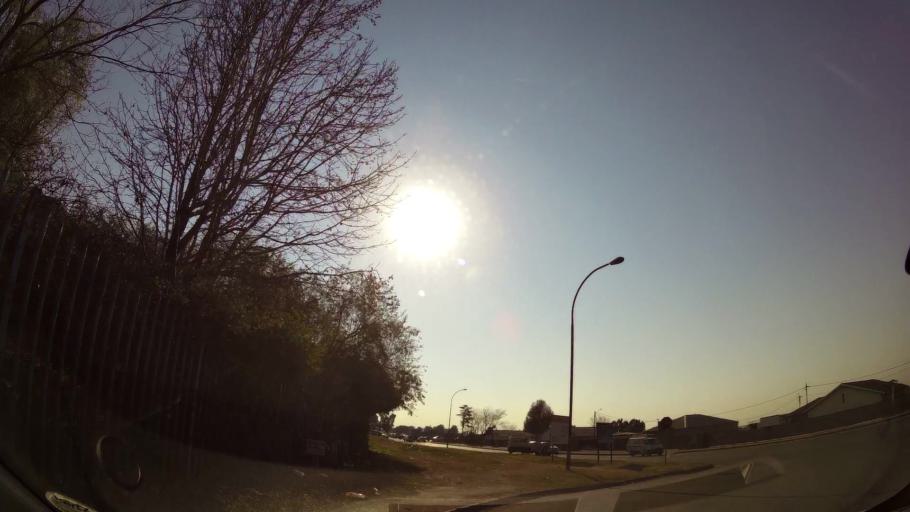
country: ZA
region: Gauteng
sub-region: Ekurhuleni Metropolitan Municipality
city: Germiston
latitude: -26.1733
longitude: 28.2006
